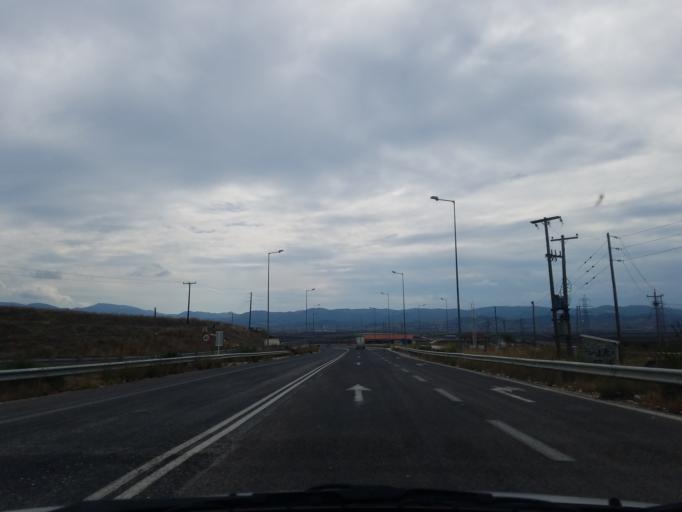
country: GR
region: Central Greece
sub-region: Nomos Fthiotidos
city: Omvriaki
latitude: 39.0866
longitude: 22.3076
